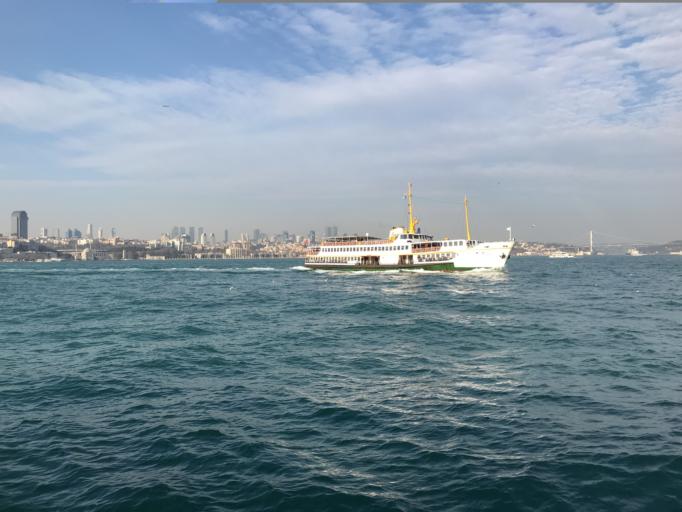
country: TR
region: Istanbul
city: Eminoenue
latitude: 41.0213
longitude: 28.9981
